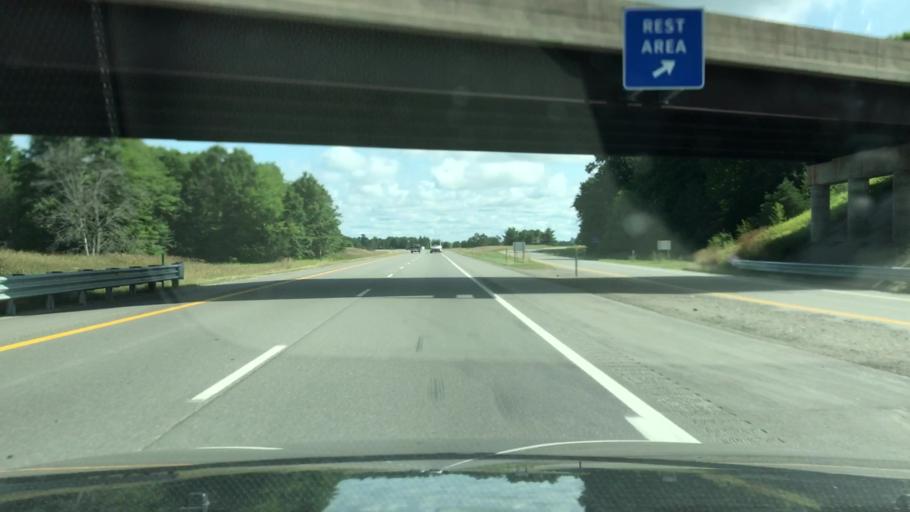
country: US
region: Michigan
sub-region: Montcalm County
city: Howard City
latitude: 43.4570
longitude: -85.4799
